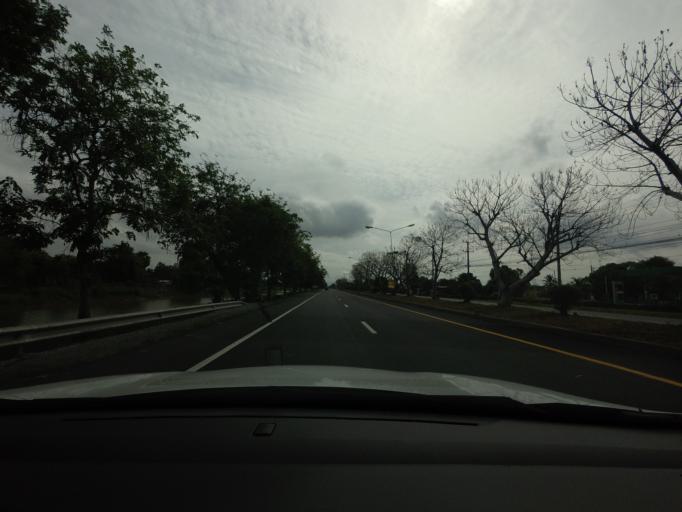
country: TH
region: Nakhon Nayok
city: Ongkharak
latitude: 14.1788
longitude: 101.0300
